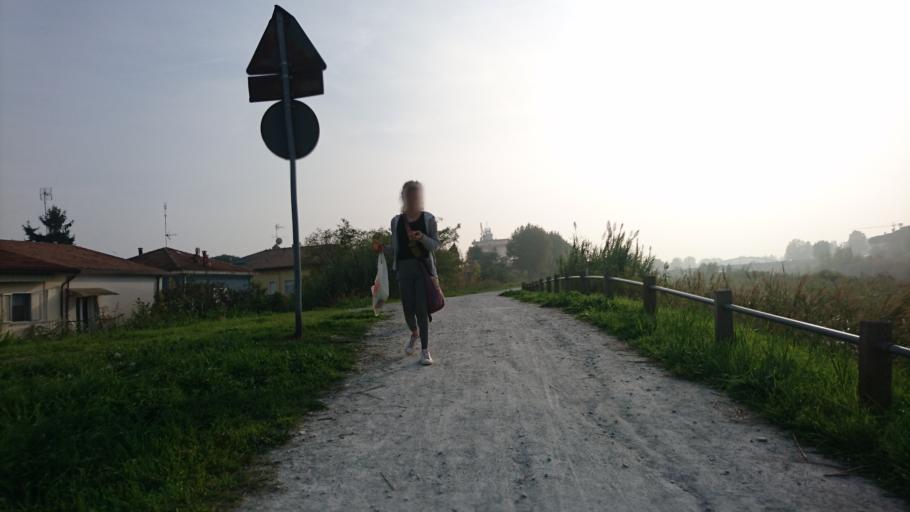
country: IT
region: Emilia-Romagna
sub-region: Provincia di Rimini
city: Rimini
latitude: 44.0699
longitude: 12.5590
